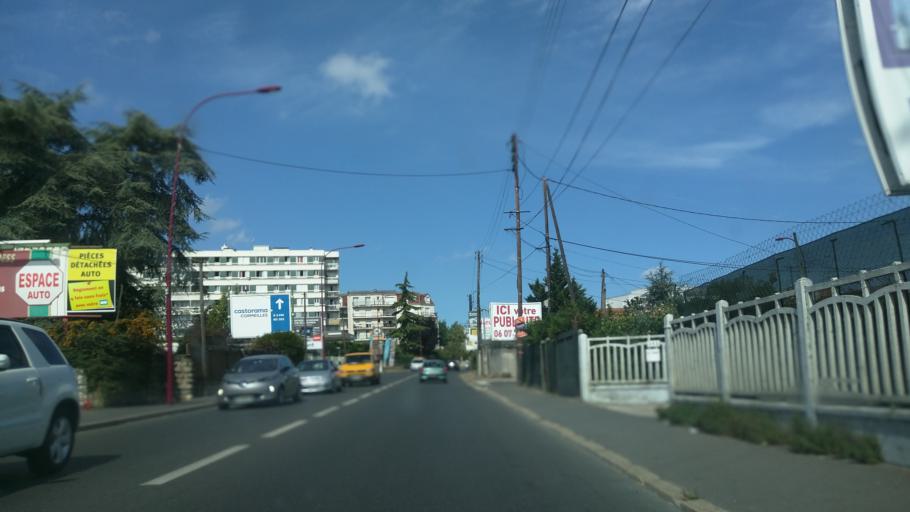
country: FR
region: Ile-de-France
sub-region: Departement du Val-d'Oise
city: Bezons
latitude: 48.9349
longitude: 2.2086
